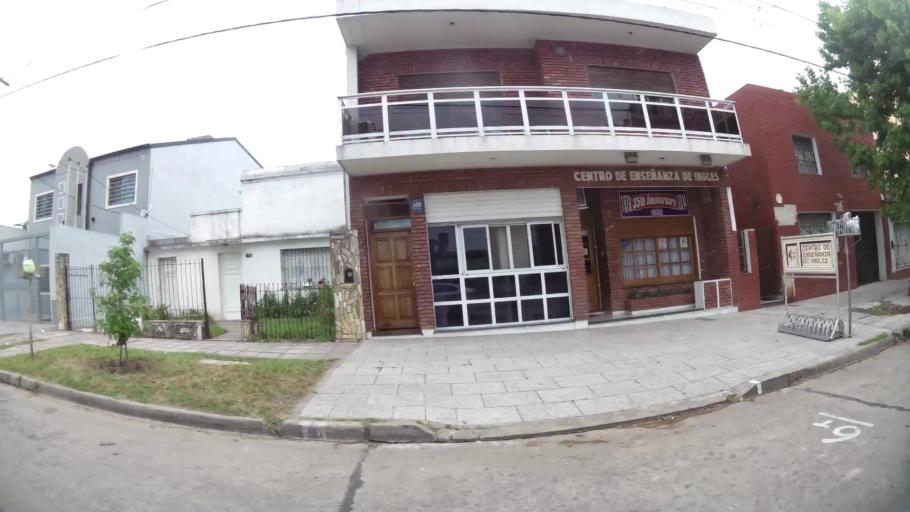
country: AR
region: Buenos Aires
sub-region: Partido de Campana
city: Campana
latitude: -34.1704
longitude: -58.9536
